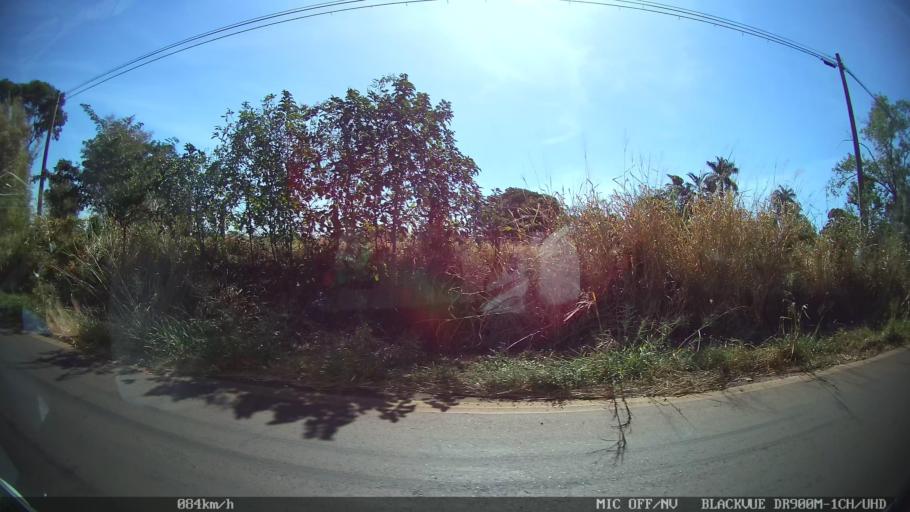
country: BR
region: Sao Paulo
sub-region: Barretos
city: Barretos
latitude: -20.5295
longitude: -48.5946
